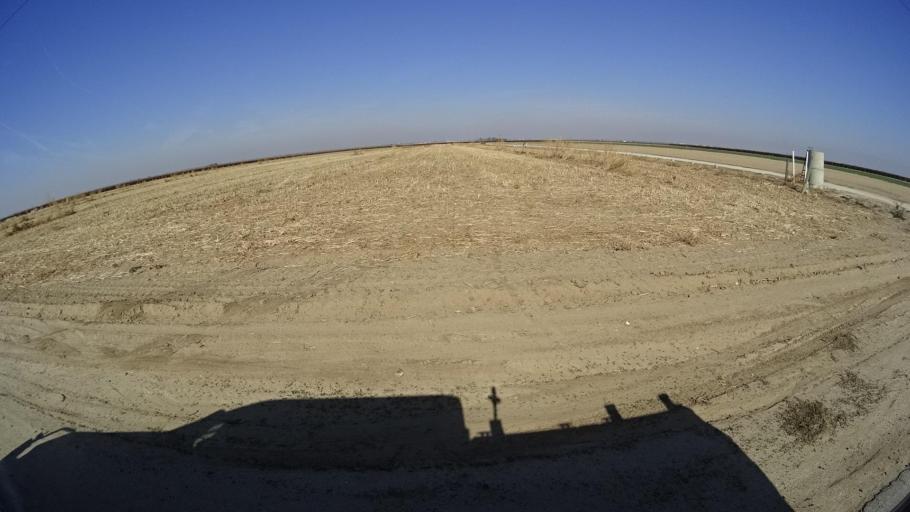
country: US
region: California
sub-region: Kern County
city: McFarland
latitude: 35.7035
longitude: -119.1806
